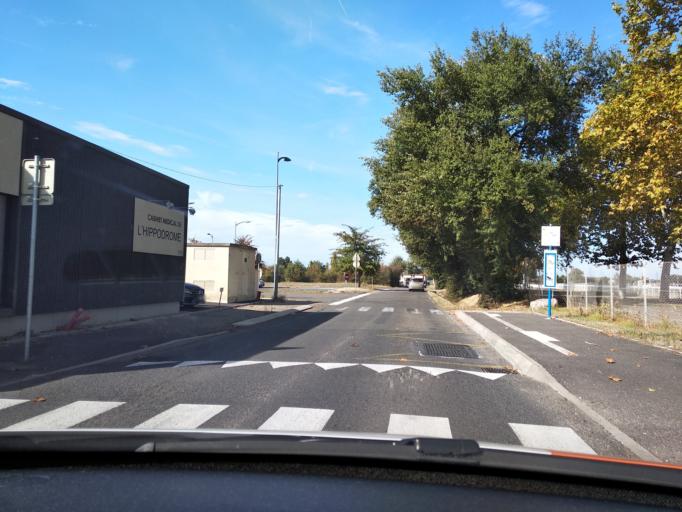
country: FR
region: Midi-Pyrenees
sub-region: Departement du Tarn-et-Garonne
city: Montauban
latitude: 44.0381
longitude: 1.3391
